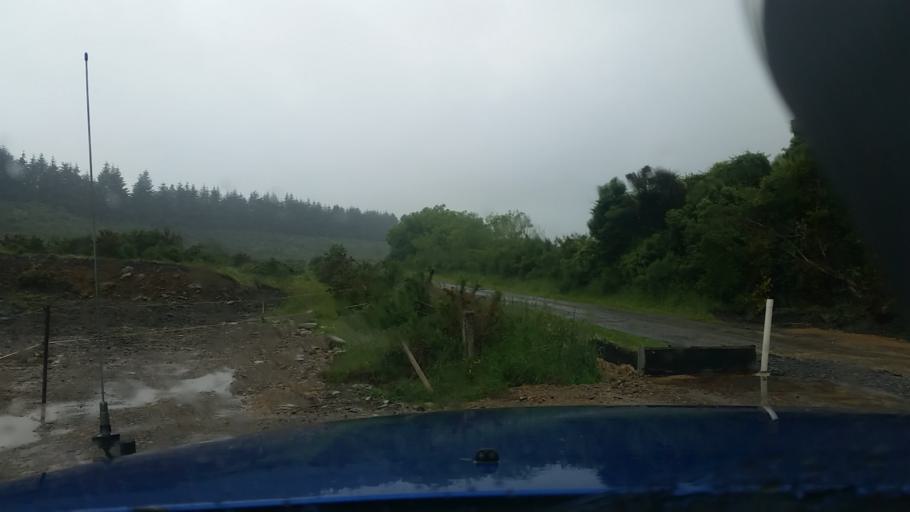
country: NZ
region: Canterbury
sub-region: Ashburton District
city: Methven
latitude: -43.5763
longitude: 171.5261
